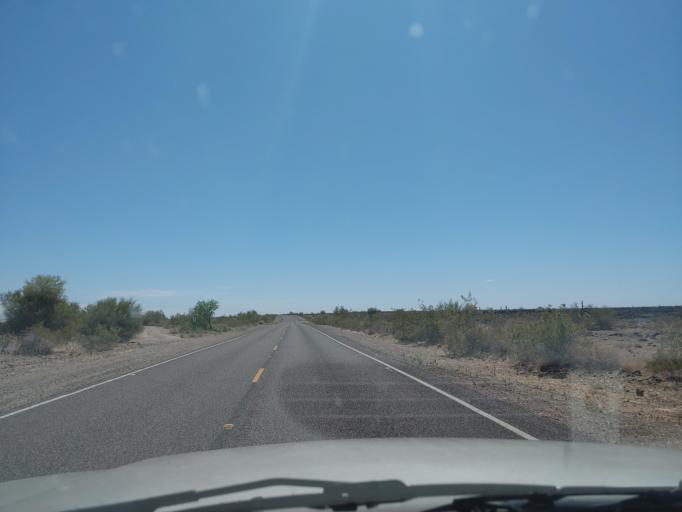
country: US
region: Arizona
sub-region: Maricopa County
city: Gila Bend
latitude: 32.9278
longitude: -113.2947
